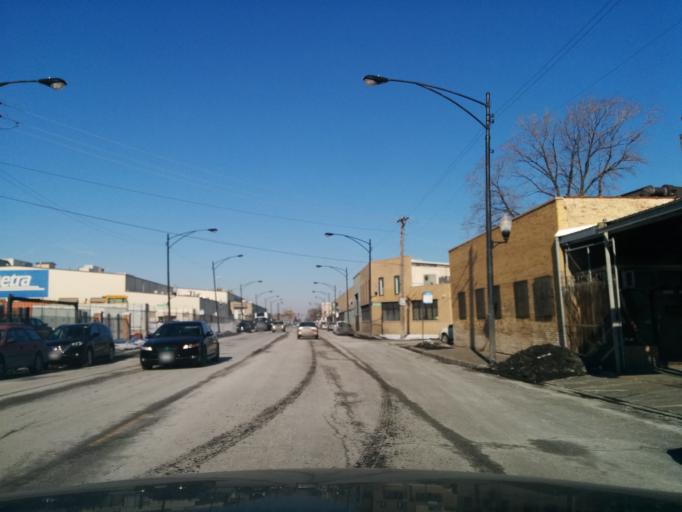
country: US
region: Illinois
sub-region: Cook County
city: Chicago
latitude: 41.8950
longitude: -87.6984
